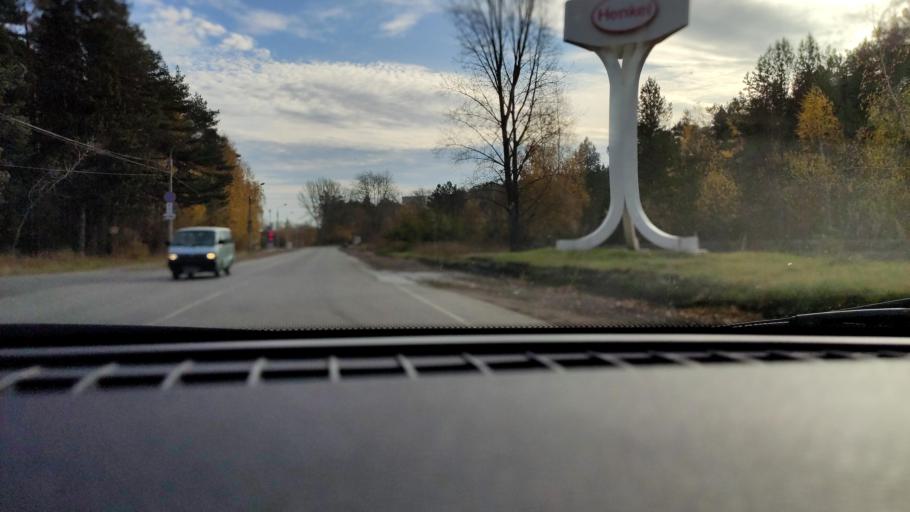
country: RU
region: Perm
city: Overyata
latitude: 58.0131
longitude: 55.9191
